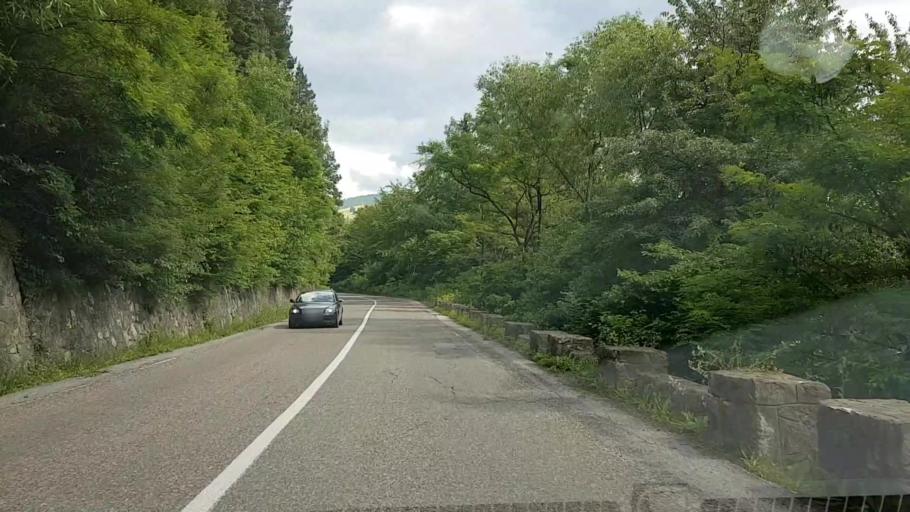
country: RO
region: Neamt
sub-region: Comuna Ceahlau
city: Ceahlau
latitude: 47.0554
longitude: 25.9715
